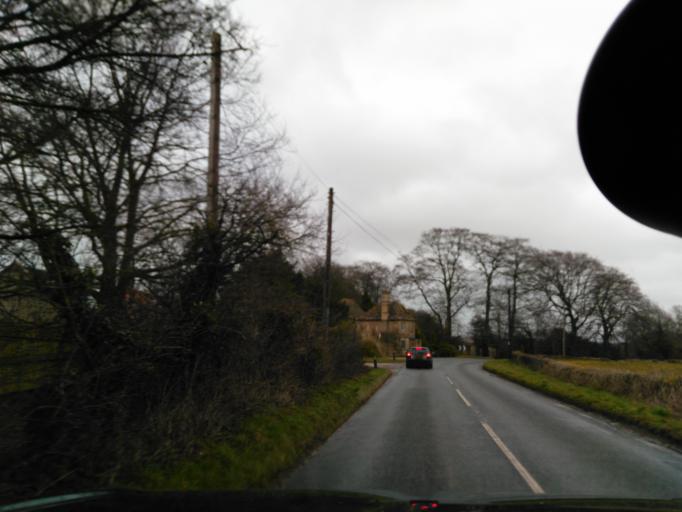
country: GB
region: England
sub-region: Wiltshire
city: Box
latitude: 51.4045
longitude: -2.2444
